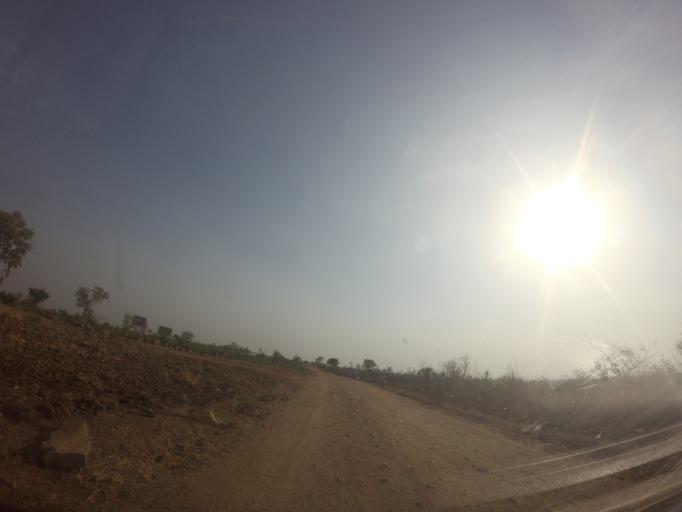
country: UG
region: Northern Region
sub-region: Maracha District
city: Maracha
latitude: 3.1193
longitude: 31.1578
